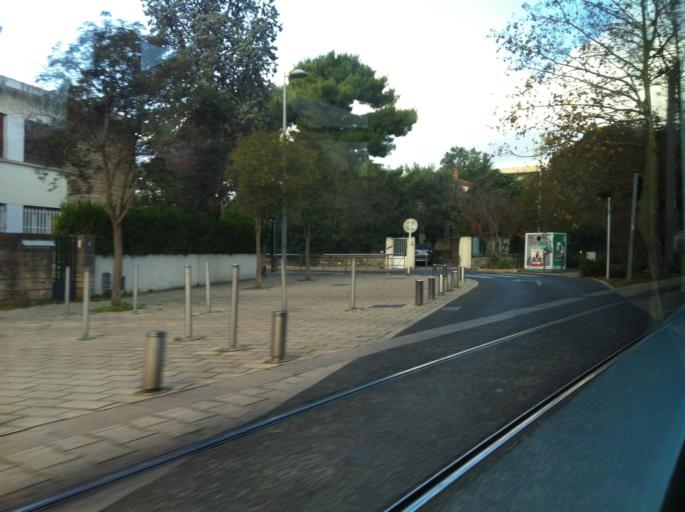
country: FR
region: Languedoc-Roussillon
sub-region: Departement de l'Herault
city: Montpellier
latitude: 43.6281
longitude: 3.8642
